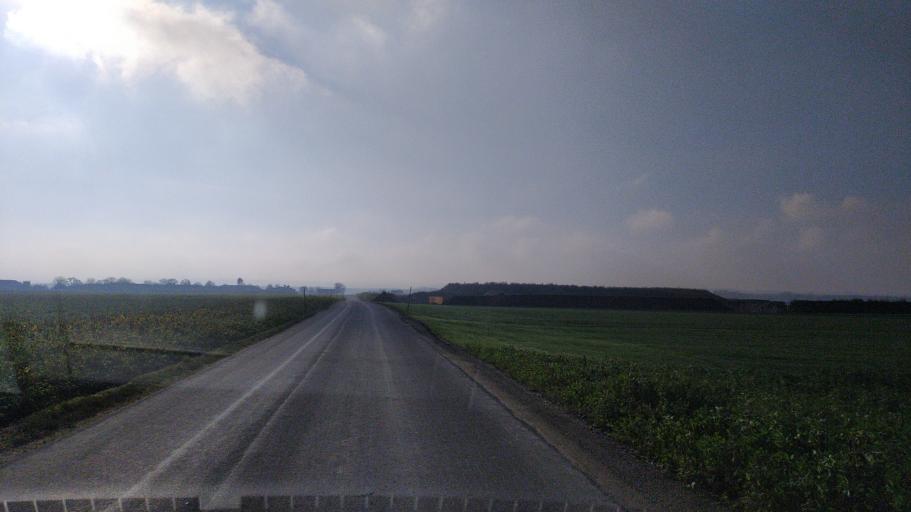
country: AT
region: Upper Austria
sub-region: Politischer Bezirk Perg
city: Perg
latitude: 48.2032
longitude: 14.6515
